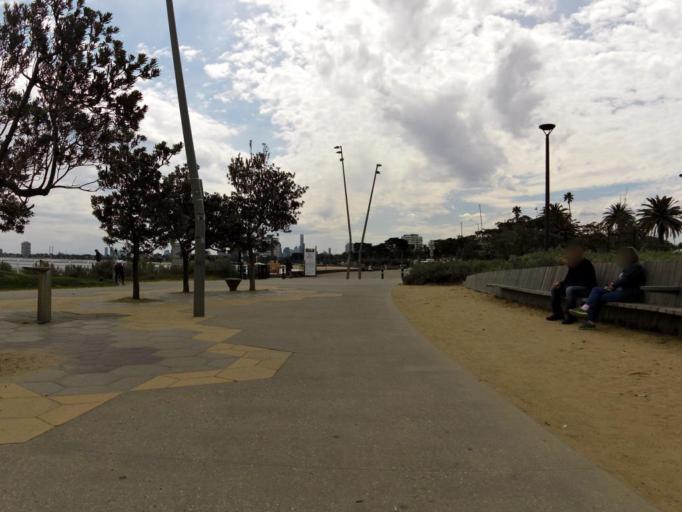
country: AU
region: Victoria
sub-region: Port Phillip
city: St Kilda West
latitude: -37.8647
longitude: 144.9710
